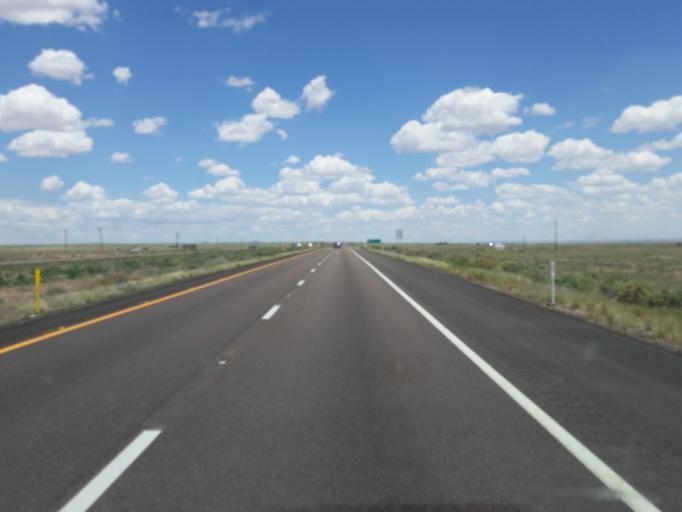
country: US
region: Arizona
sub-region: Navajo County
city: Holbrook
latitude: 34.9827
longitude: -110.0427
